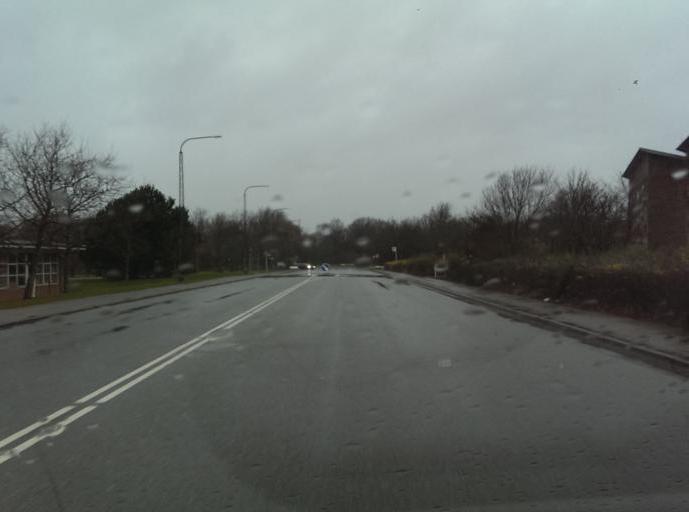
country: DK
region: South Denmark
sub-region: Esbjerg Kommune
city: Esbjerg
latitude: 55.5070
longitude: 8.4406
